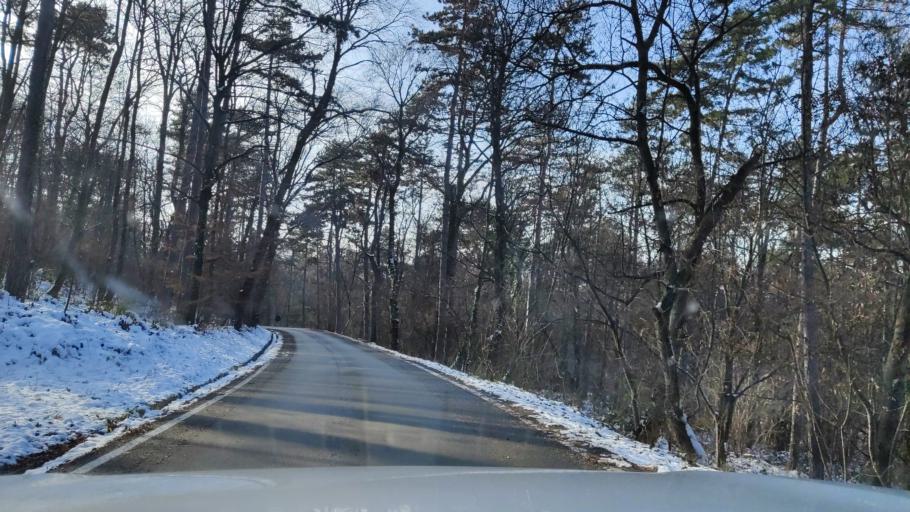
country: RS
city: Rusanj
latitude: 44.6987
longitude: 20.5078
